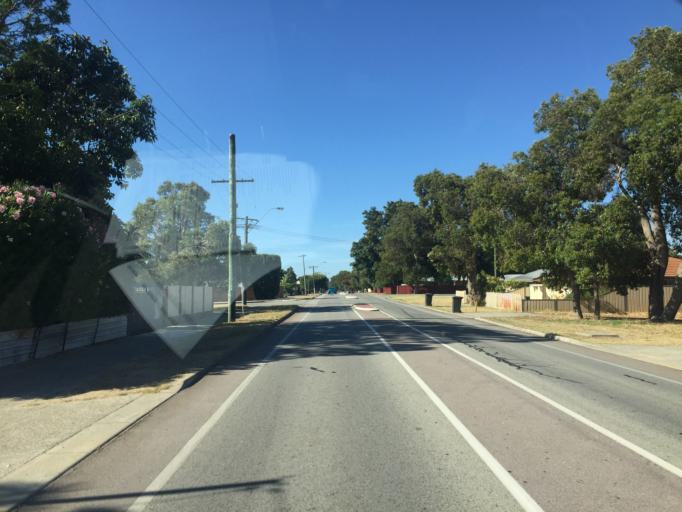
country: AU
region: Western Australia
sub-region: Gosnells
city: Maddington
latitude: -32.0372
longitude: 115.9821
